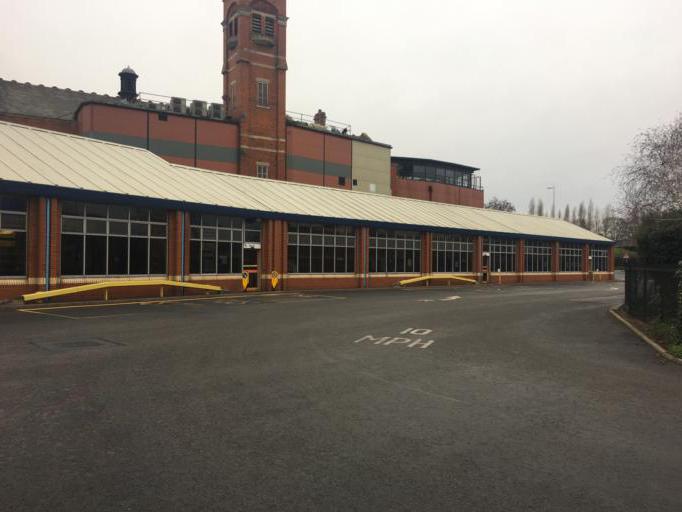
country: GB
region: England
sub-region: Coventry
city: Coventry
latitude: 52.4102
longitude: -1.5074
